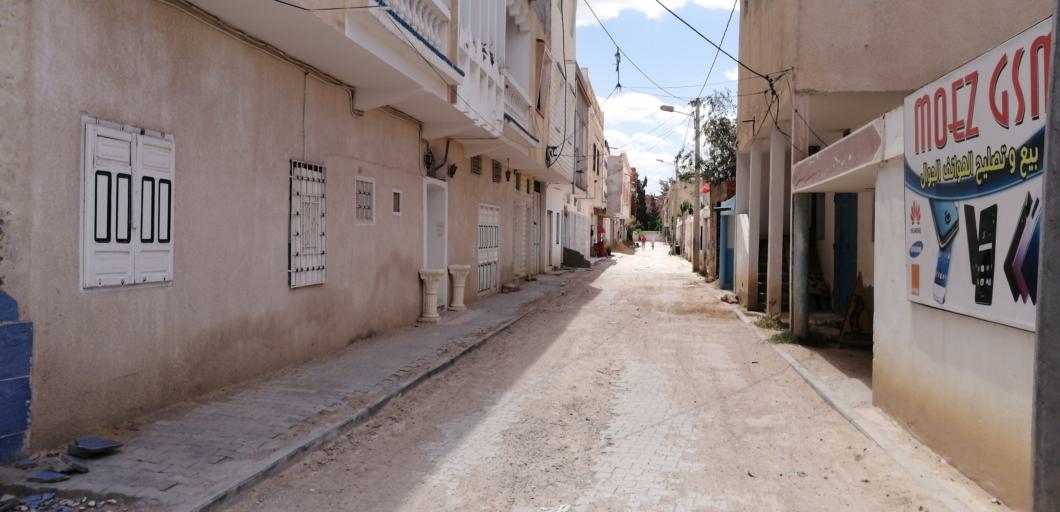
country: TN
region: Al Qayrawan
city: Kairouan
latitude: 35.6169
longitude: 9.9281
